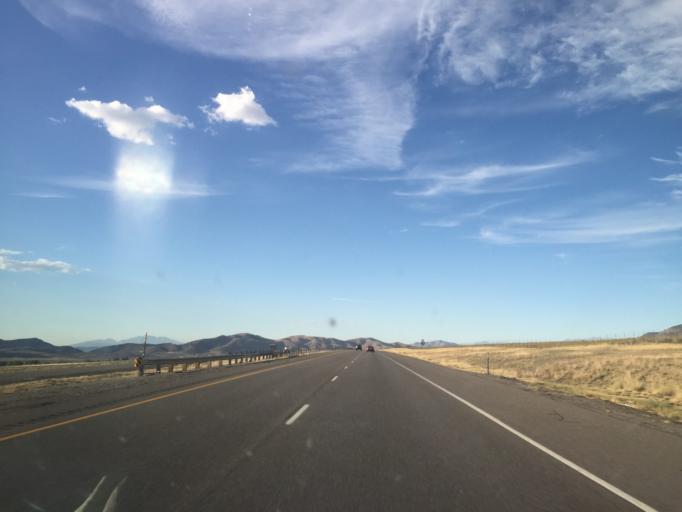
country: US
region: Utah
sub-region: Juab County
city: Mona
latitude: 39.8285
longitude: -111.8338
